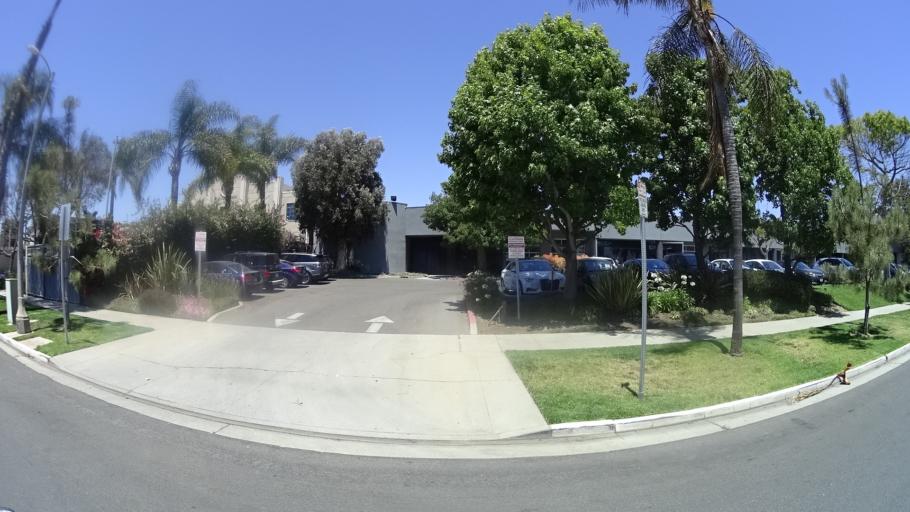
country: US
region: California
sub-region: Los Angeles County
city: Santa Monica
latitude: 34.0224
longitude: -118.4800
